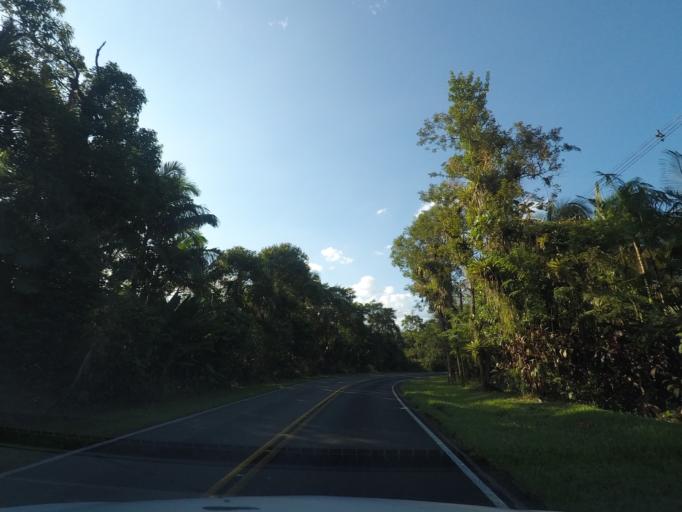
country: BR
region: Parana
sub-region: Antonina
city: Antonina
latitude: -25.4203
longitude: -48.8751
